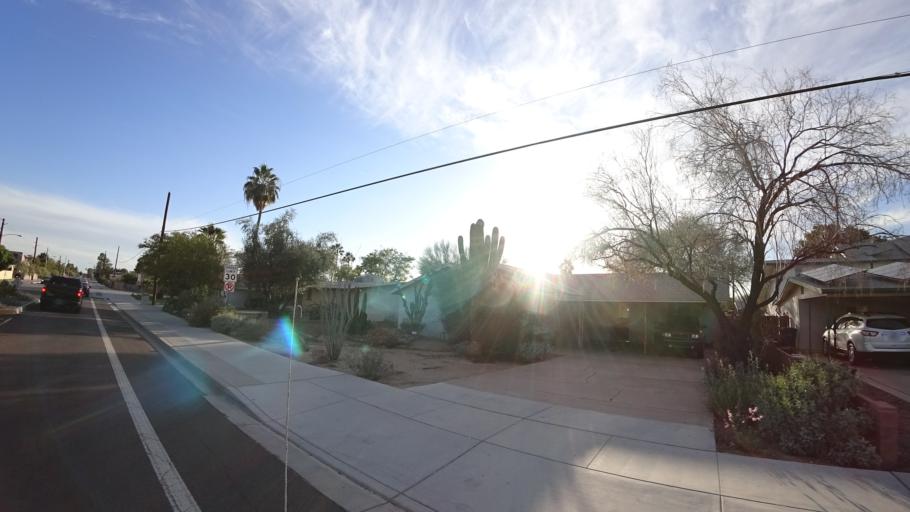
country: US
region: Arizona
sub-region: Maricopa County
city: Tempe Junction
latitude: 33.4175
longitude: -111.9522
